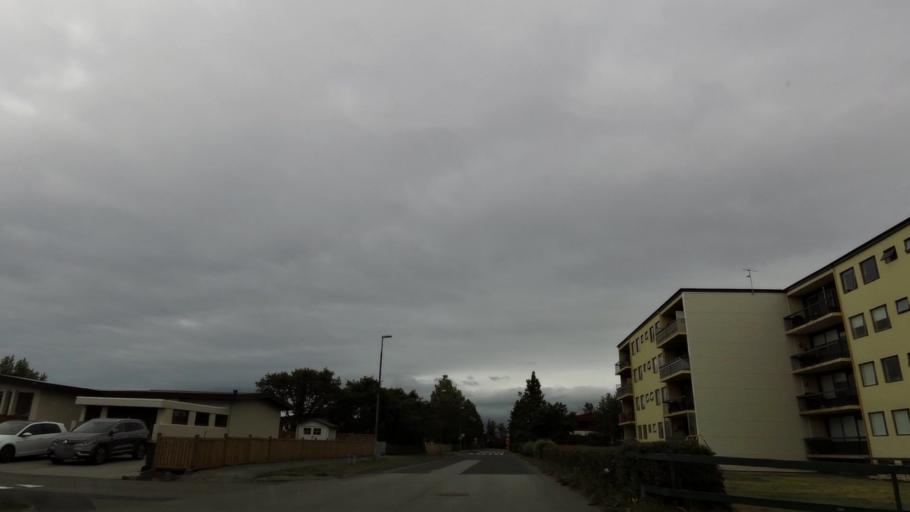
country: IS
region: Capital Region
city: Hafnarfjoerdur
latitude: 64.0809
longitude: -21.9613
